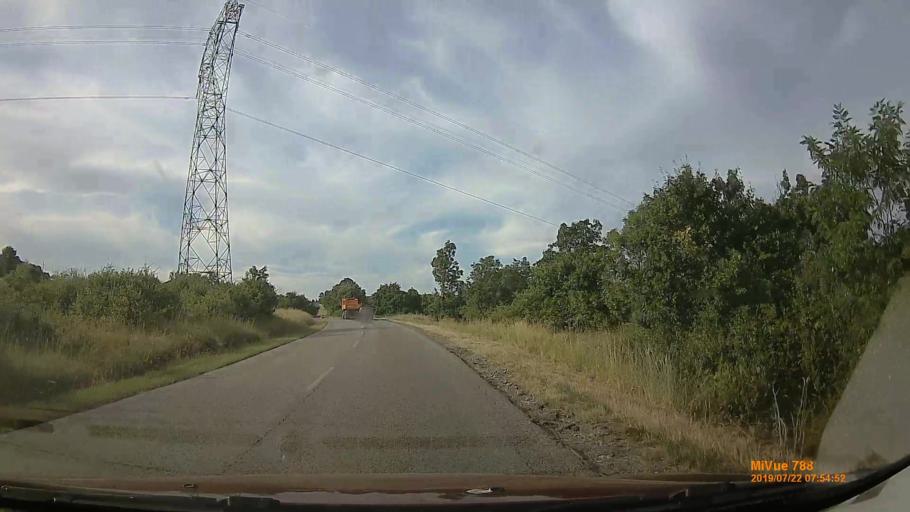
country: HU
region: Veszprem
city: Ajka
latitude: 47.0358
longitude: 17.5567
